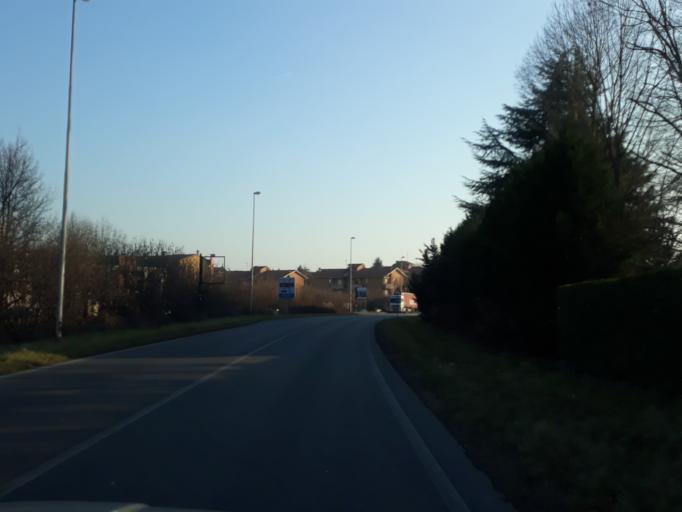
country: IT
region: Lombardy
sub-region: Provincia di Monza e Brianza
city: Bellusco
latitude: 45.6215
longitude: 9.4224
